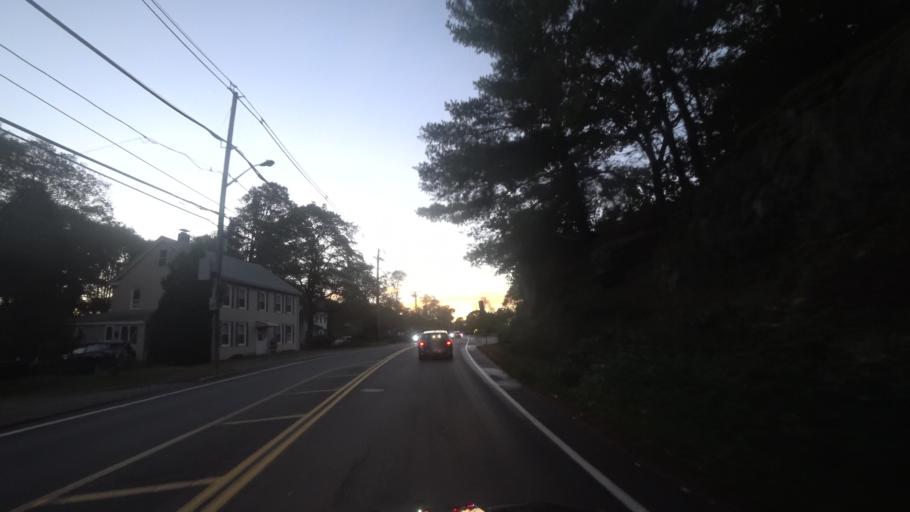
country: US
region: Massachusetts
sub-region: Essex County
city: Saugus
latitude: 42.4721
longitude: -71.0347
